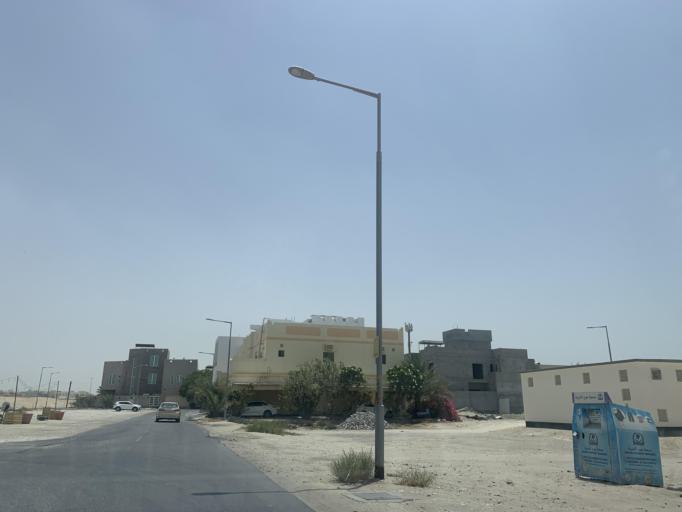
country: BH
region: Central Governorate
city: Madinat Hamad
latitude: 26.1475
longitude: 50.5039
